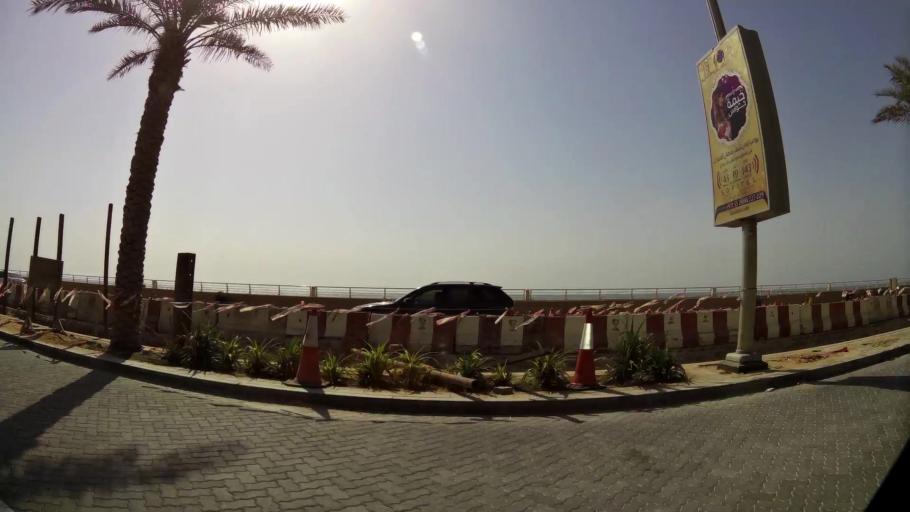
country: AE
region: Dubai
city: Dubai
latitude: 25.1299
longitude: 55.1148
